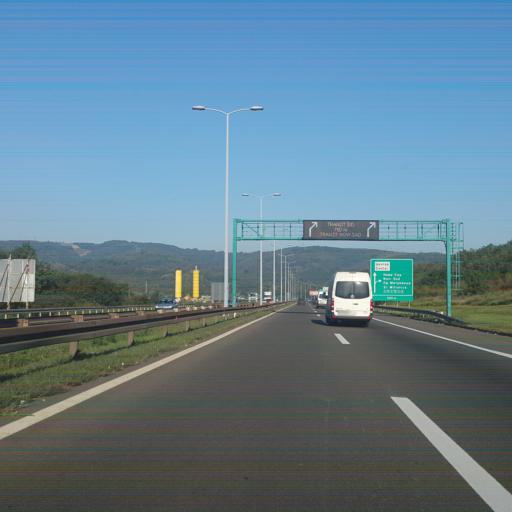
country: RS
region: Central Serbia
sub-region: Belgrade
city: Zvezdara
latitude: 44.7205
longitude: 20.5496
